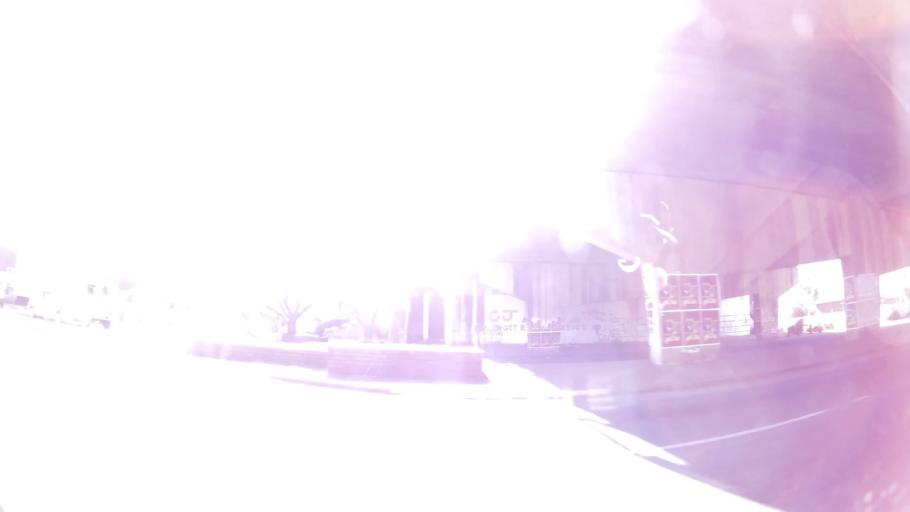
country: ZA
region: Gauteng
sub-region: West Rand District Municipality
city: Carletonville
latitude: -26.3445
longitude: 27.3902
